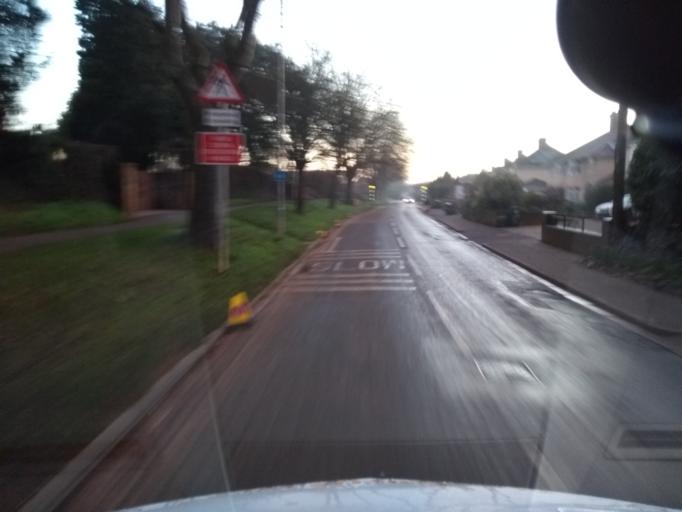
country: GB
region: England
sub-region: Somerset
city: Bridgwater
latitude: 51.1227
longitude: -3.0228
